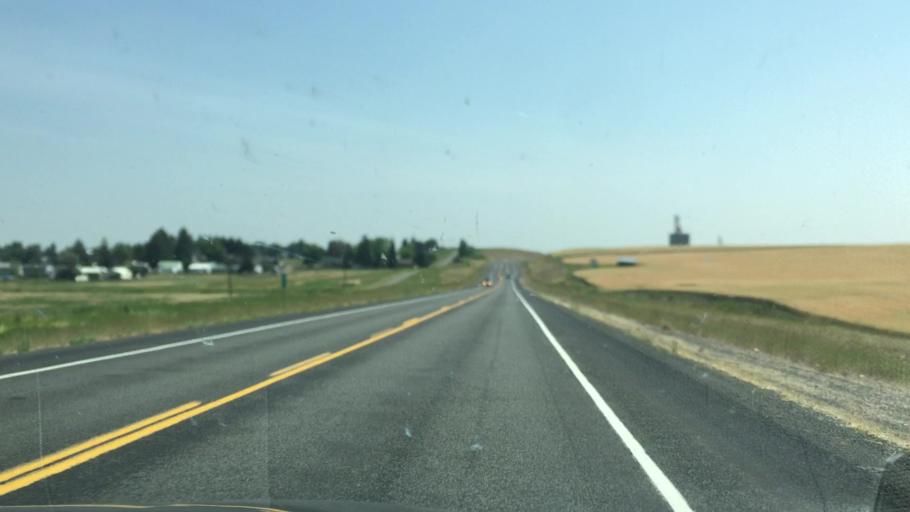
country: US
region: Idaho
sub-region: Lewis County
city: Nezperce
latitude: 46.2377
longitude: -116.4799
